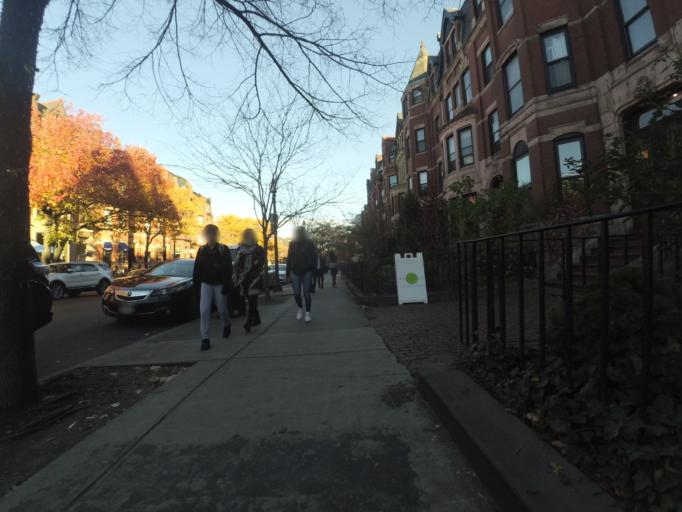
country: US
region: Massachusetts
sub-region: Suffolk County
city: Boston
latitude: 42.3493
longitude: -71.0832
